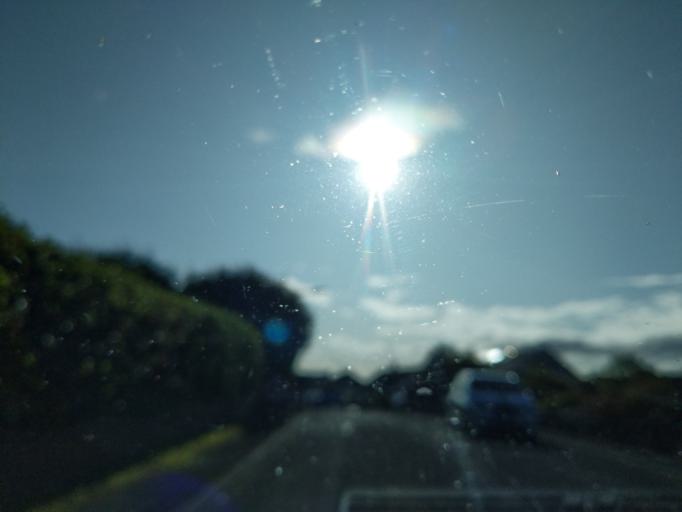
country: GB
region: Scotland
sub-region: Dumfries and Galloway
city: Kirkcudbright
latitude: 54.8338
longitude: -4.0481
